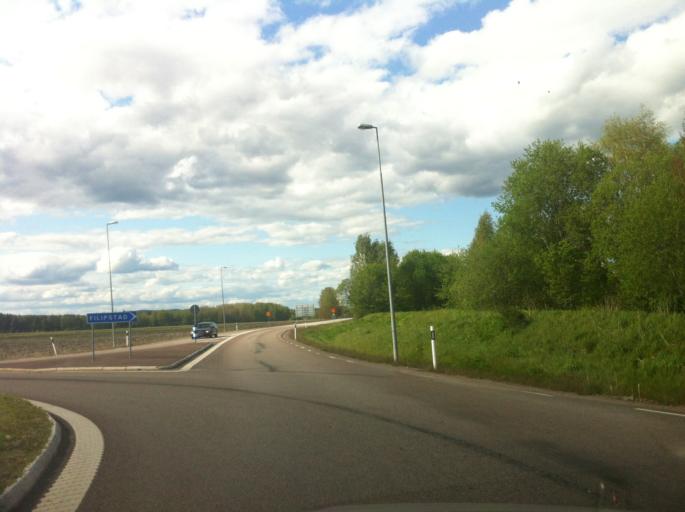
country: SE
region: Vaermland
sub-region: Storfors Kommun
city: Storfors
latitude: 59.5446
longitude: 14.2780
